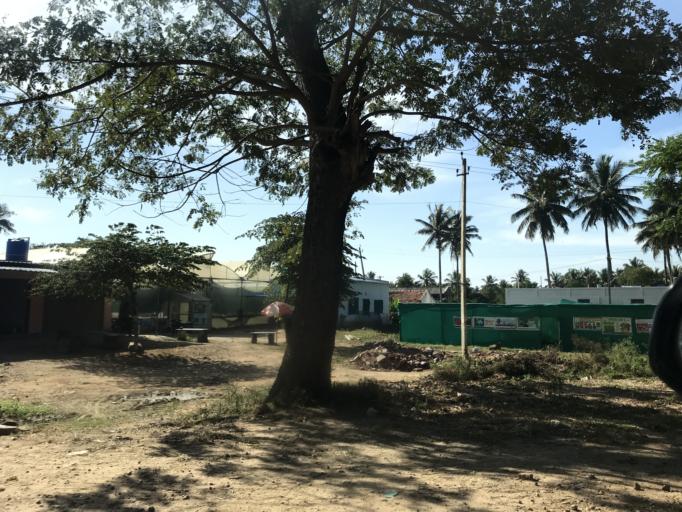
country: IN
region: Karnataka
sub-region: Mysore
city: Mysore
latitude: 12.2104
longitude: 76.5605
